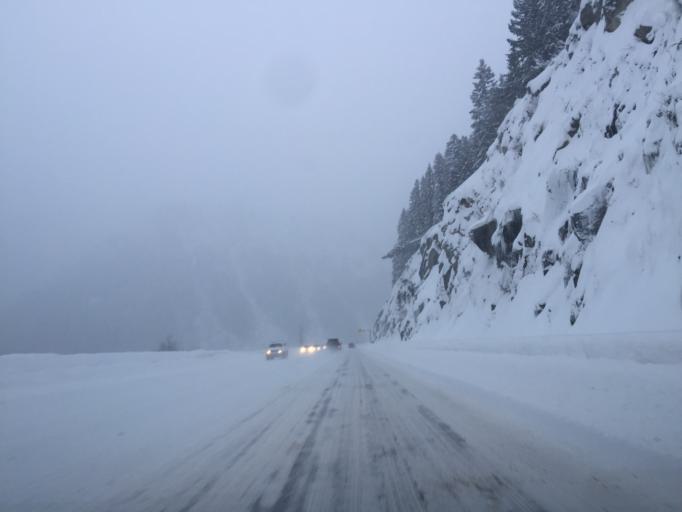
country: US
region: Washington
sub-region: Chelan County
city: Leavenworth
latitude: 47.7429
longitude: -121.1241
